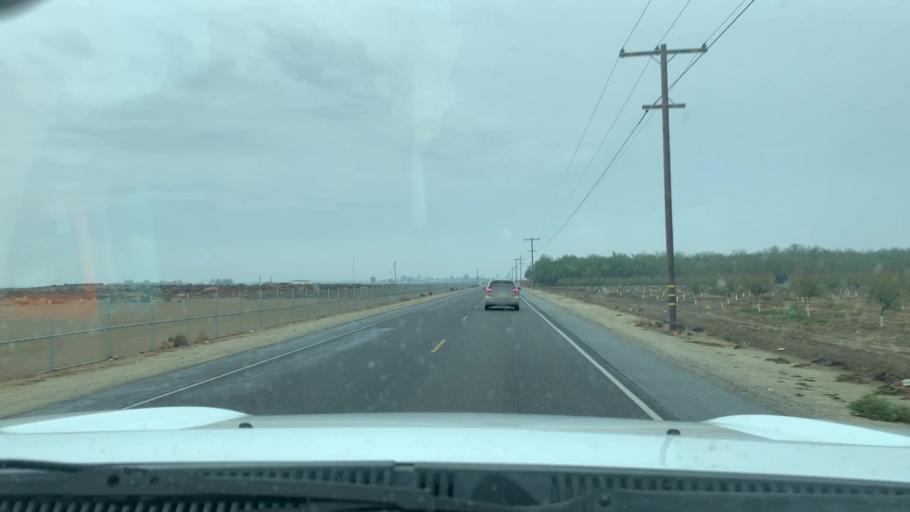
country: US
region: California
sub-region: Kern County
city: Delano
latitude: 35.7613
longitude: -119.3160
